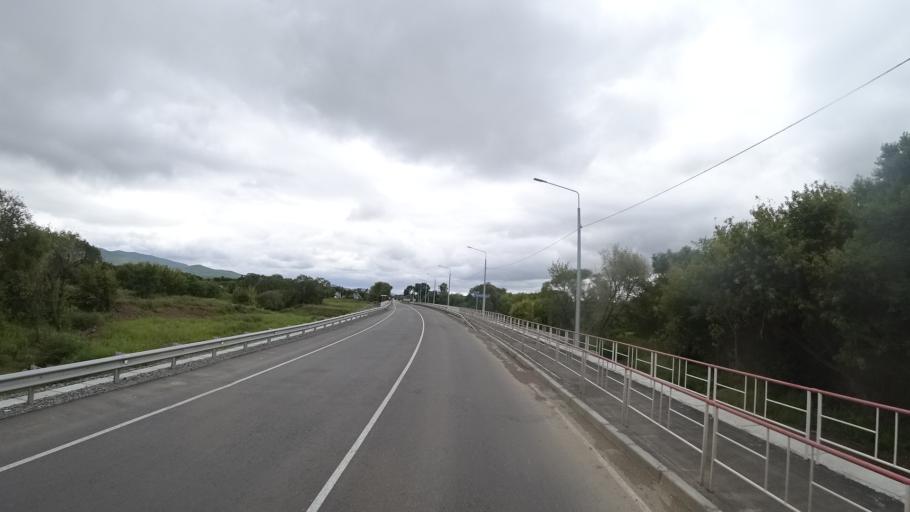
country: RU
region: Primorskiy
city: Chernigovka
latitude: 44.3431
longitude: 132.5916
